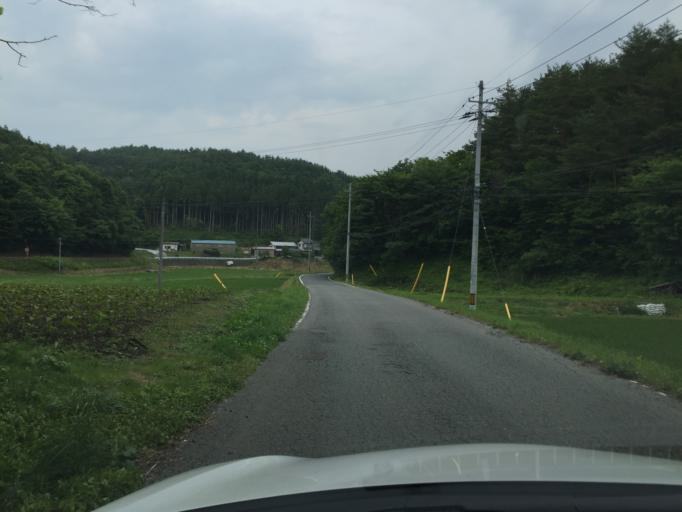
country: JP
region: Fukushima
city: Iwaki
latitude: 37.1632
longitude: 140.7054
